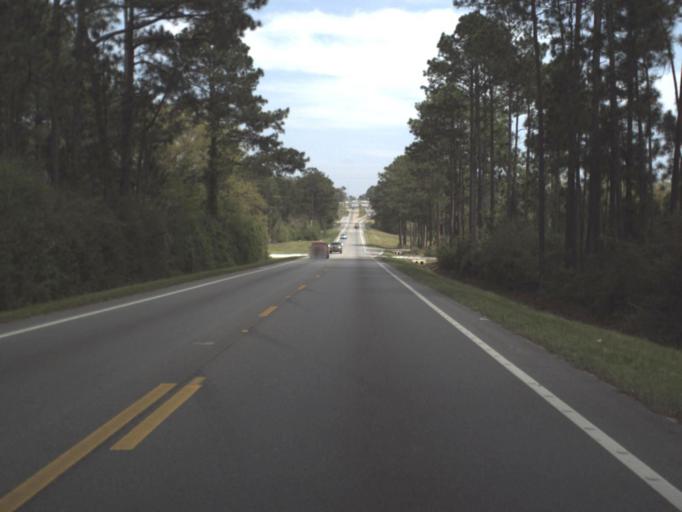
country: US
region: Florida
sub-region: Escambia County
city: Gonzalez
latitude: 30.5349
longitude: -87.3482
